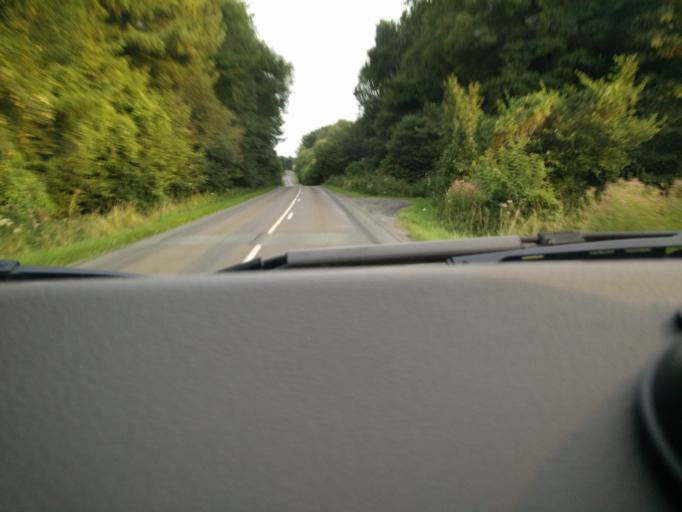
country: FR
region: Nord-Pas-de-Calais
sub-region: Departement du Nord
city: La Longueville
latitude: 50.2638
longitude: 3.8230
